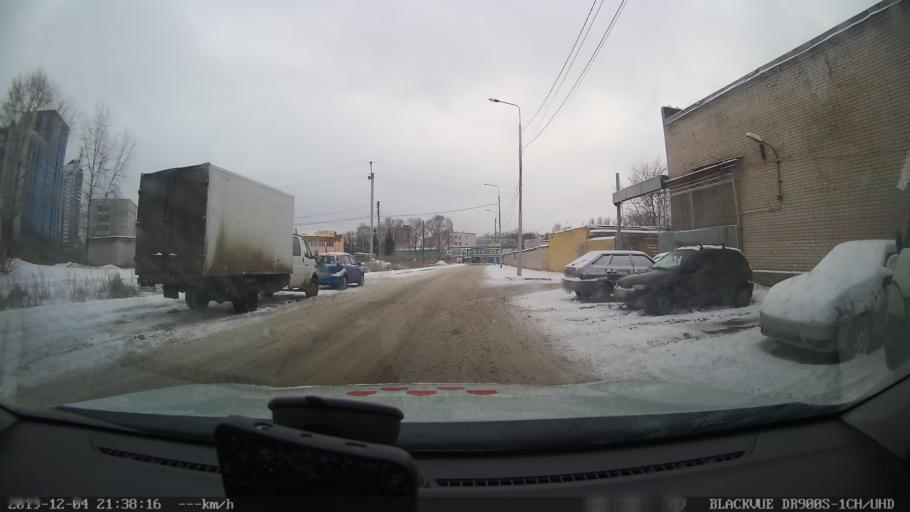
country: RU
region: Tatarstan
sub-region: Gorod Kazan'
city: Kazan
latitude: 55.7630
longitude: 49.1457
